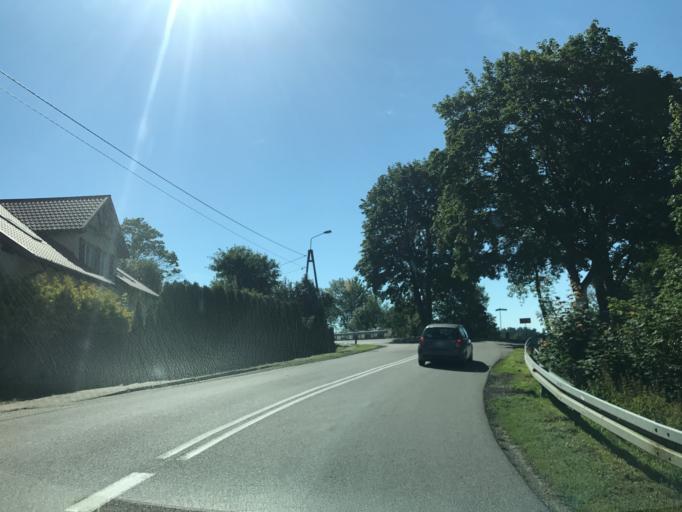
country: PL
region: Pomeranian Voivodeship
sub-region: Powiat bytowski
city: Czarna Dabrowka
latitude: 54.3555
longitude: 17.5682
